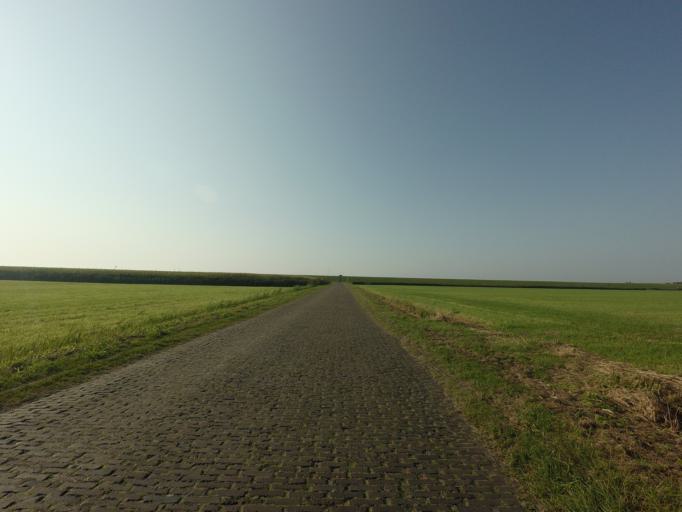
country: NL
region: Friesland
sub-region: Gemeente Schiermonnikoog
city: Schiermonnikoog
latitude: 53.4742
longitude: 6.1616
